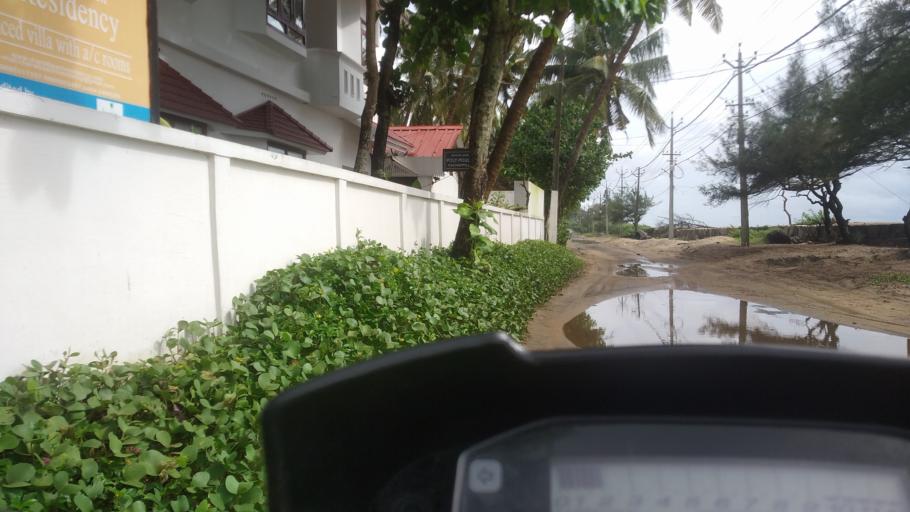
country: IN
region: Kerala
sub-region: Thrissur District
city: Kodungallur
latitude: 10.1322
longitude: 76.1813
